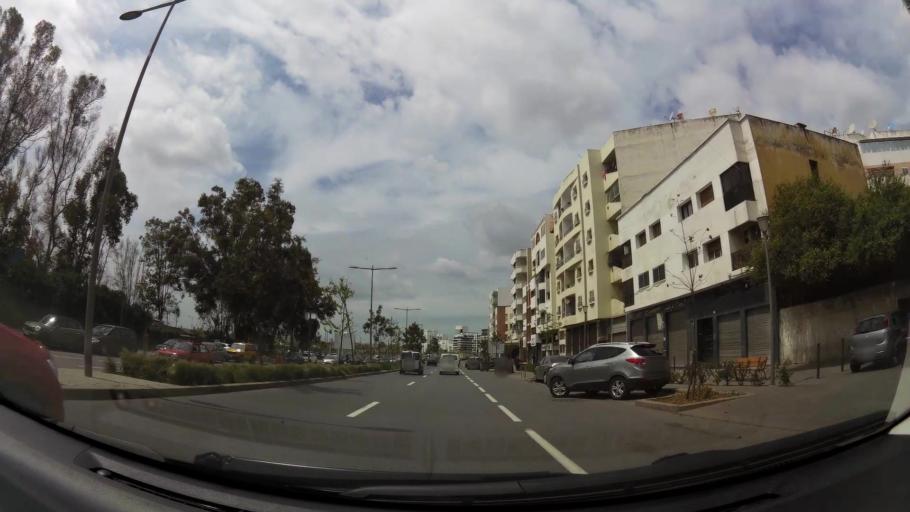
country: MA
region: Grand Casablanca
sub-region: Casablanca
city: Casablanca
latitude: 33.5660
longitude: -7.6531
